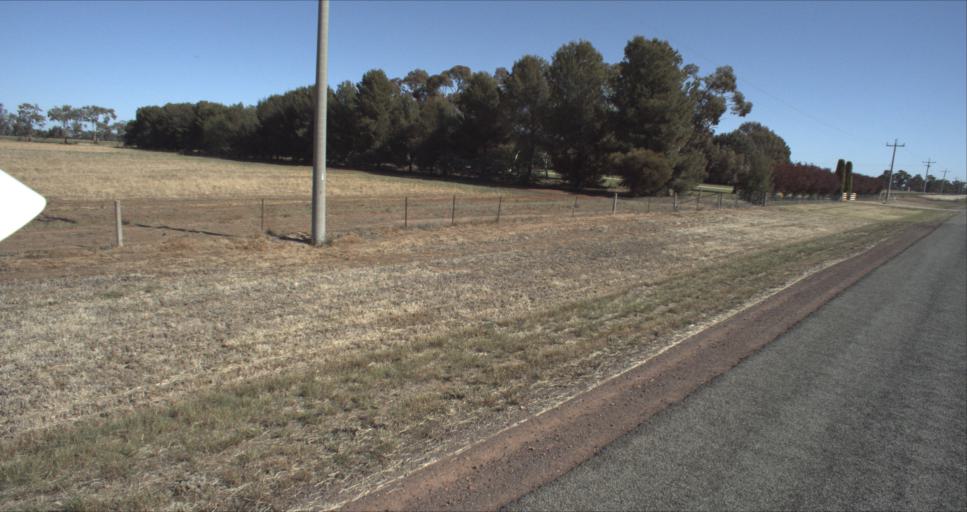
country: AU
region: New South Wales
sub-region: Leeton
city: Leeton
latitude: -34.5854
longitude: 146.2607
